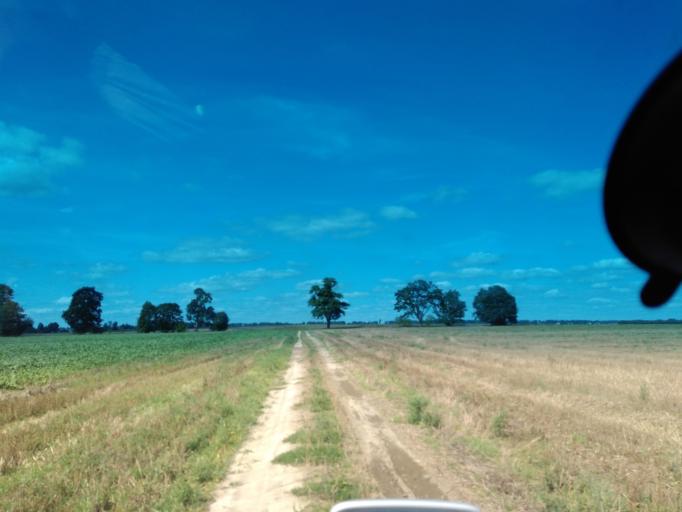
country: BY
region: Minsk
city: Stan'kava
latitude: 53.6328
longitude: 27.3260
